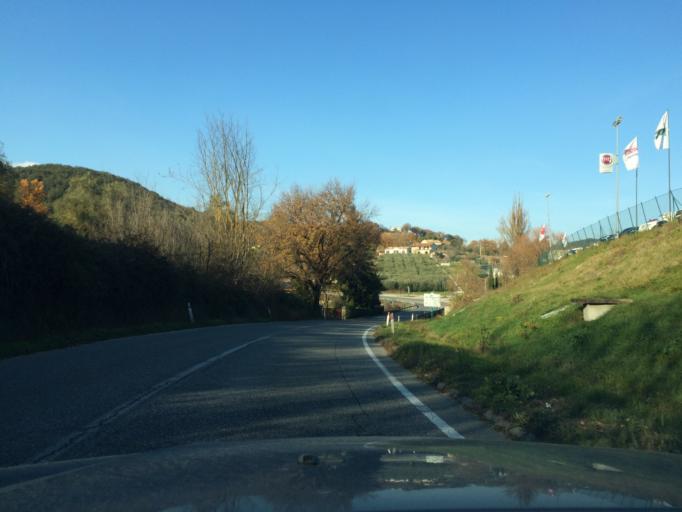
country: IT
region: Umbria
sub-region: Provincia di Terni
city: Fornole
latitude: 42.5494
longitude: 12.4474
